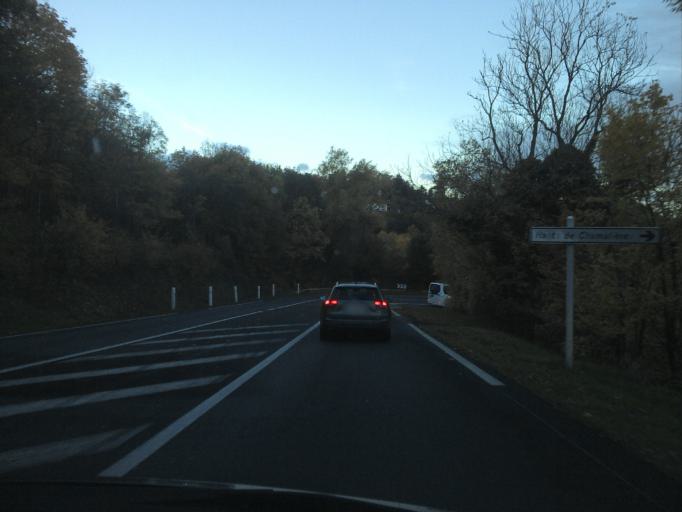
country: FR
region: Auvergne
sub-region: Departement du Puy-de-Dome
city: Durtol
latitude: 45.7848
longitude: 3.0488
